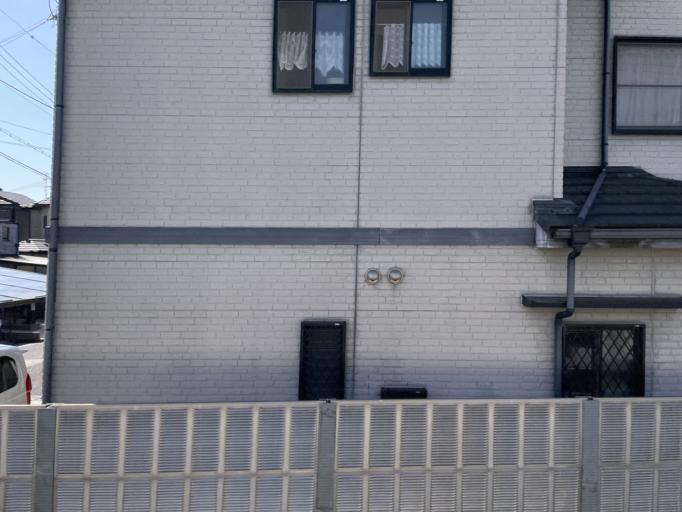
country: JP
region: Nara
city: Tenri
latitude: 34.6007
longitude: 135.8201
